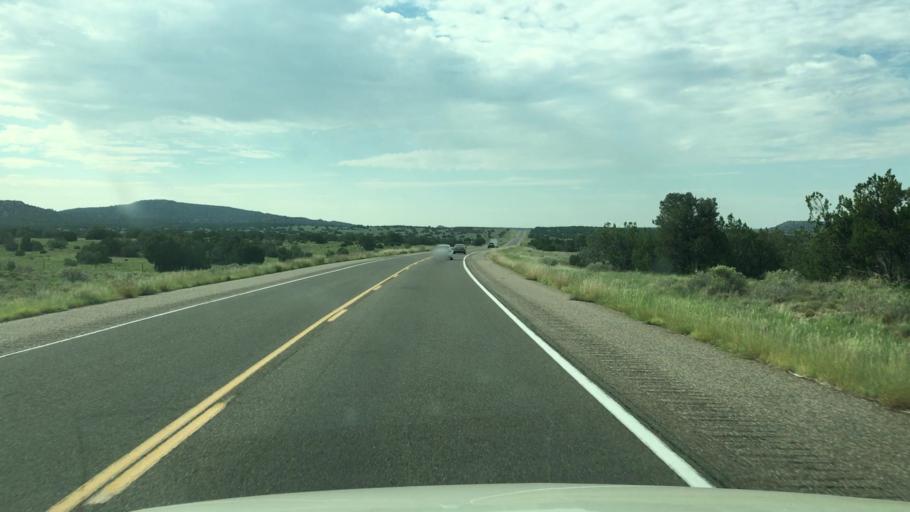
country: US
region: New Mexico
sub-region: Santa Fe County
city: Eldorado at Santa Fe
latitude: 35.3290
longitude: -105.8339
